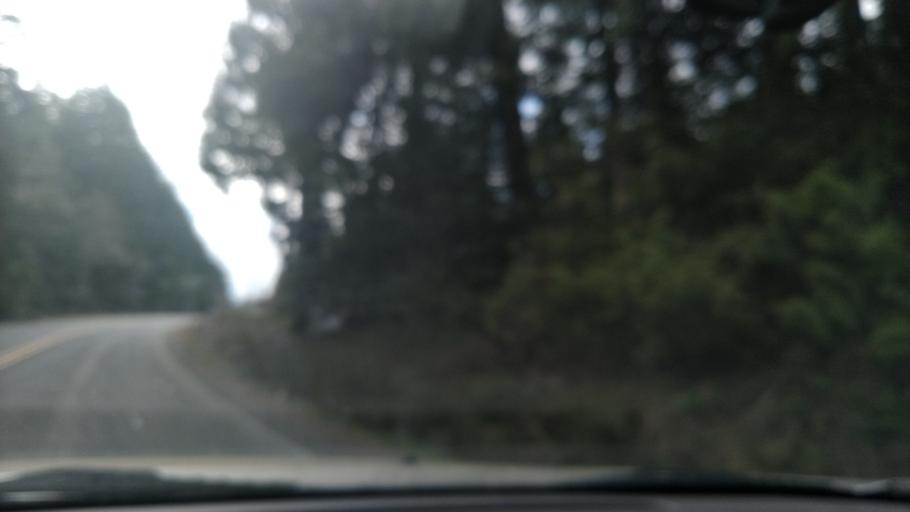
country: CA
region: British Columbia
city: Campbell River
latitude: 49.9861
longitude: -125.4152
